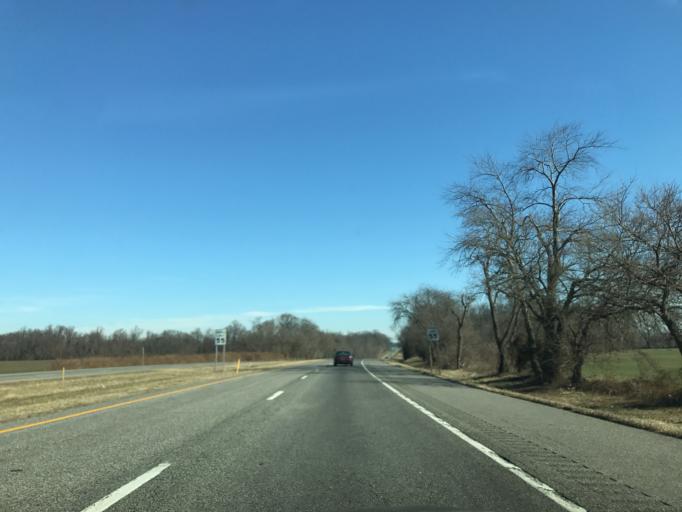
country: US
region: Delaware
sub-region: New Castle County
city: Middletown
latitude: 39.3733
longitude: -75.8120
